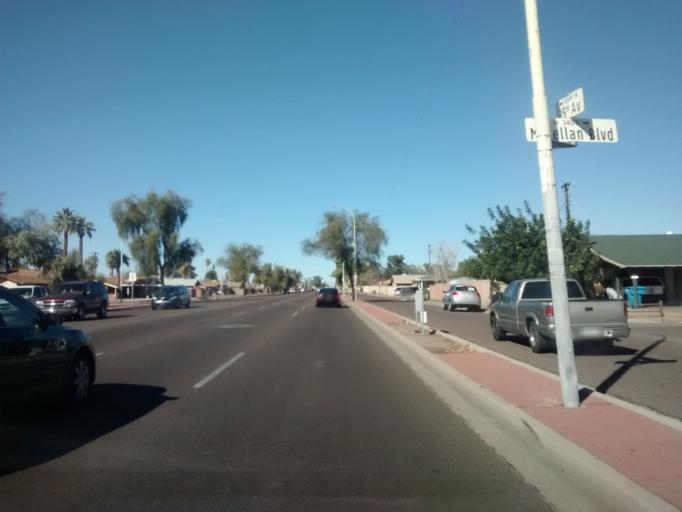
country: US
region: Arizona
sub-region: Maricopa County
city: Glendale
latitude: 33.5324
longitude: -112.1342
